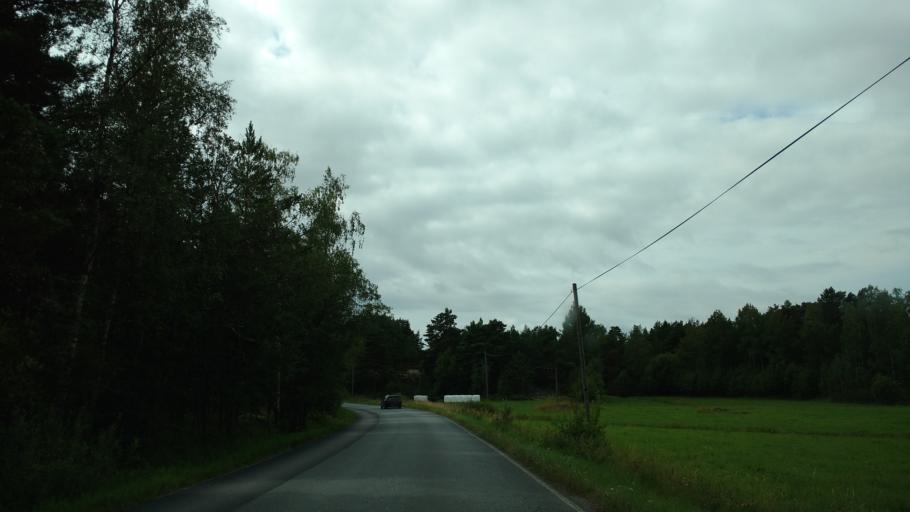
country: FI
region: Varsinais-Suomi
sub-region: Aboland-Turunmaa
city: Dragsfjaerd
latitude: 59.9648
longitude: 22.4301
